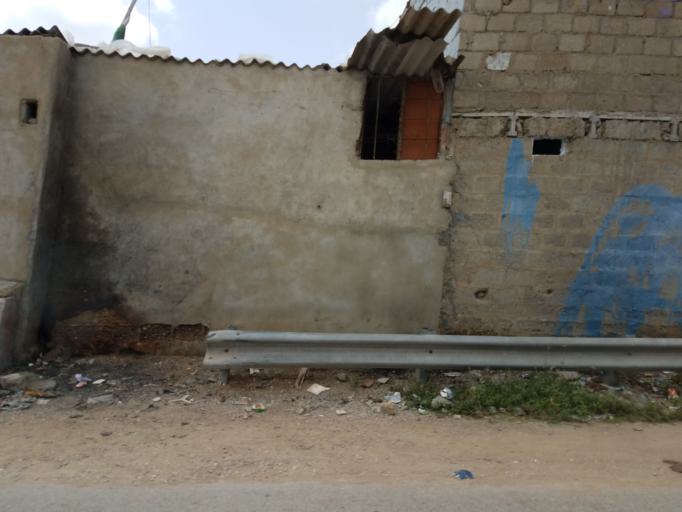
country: PK
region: Sindh
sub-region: Karachi District
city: Karachi
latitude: 24.9418
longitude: 67.0886
